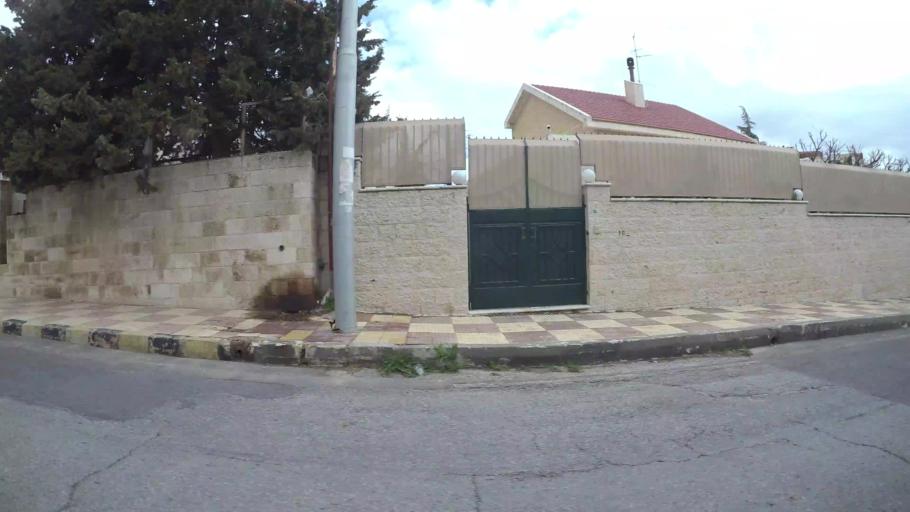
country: JO
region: Amman
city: Wadi as Sir
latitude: 31.9857
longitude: 35.8403
